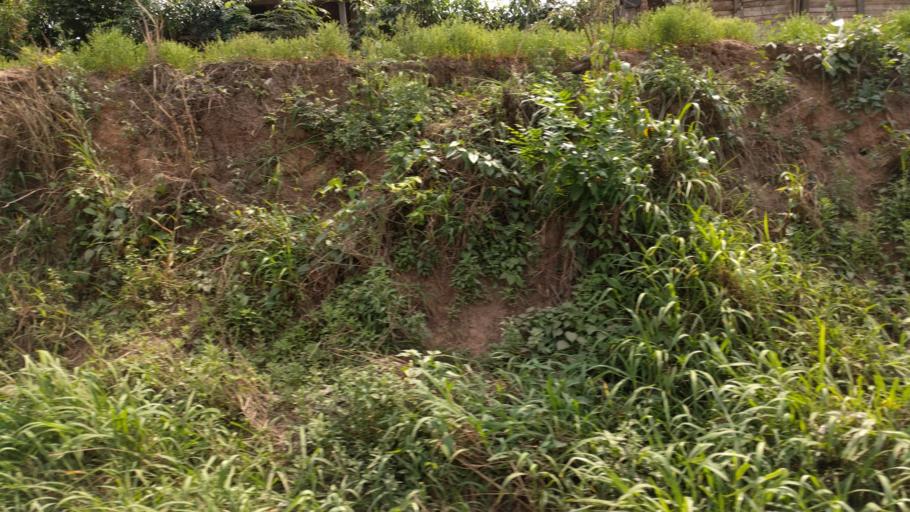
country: BO
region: Santa Cruz
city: Limoncito
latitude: -18.0325
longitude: -63.4047
